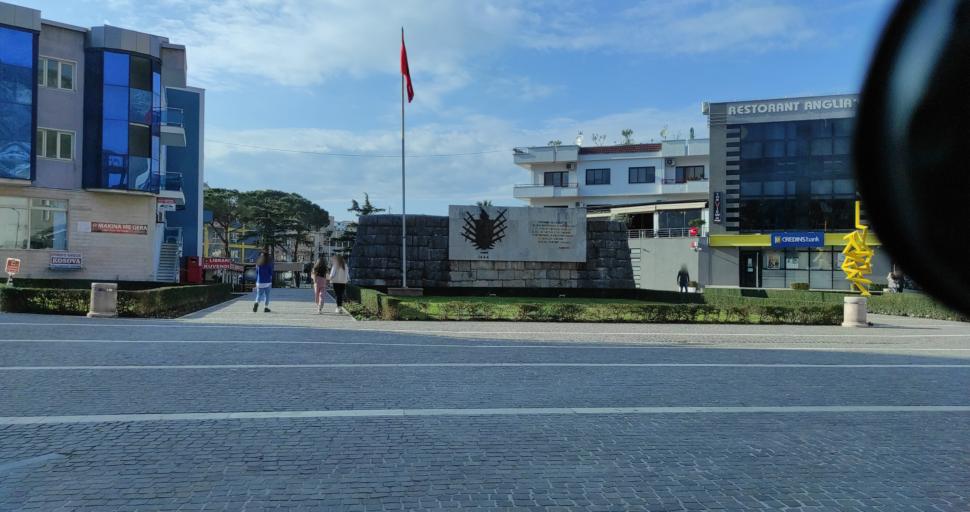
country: AL
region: Lezhe
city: Lezhe
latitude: 41.7805
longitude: 19.6448
